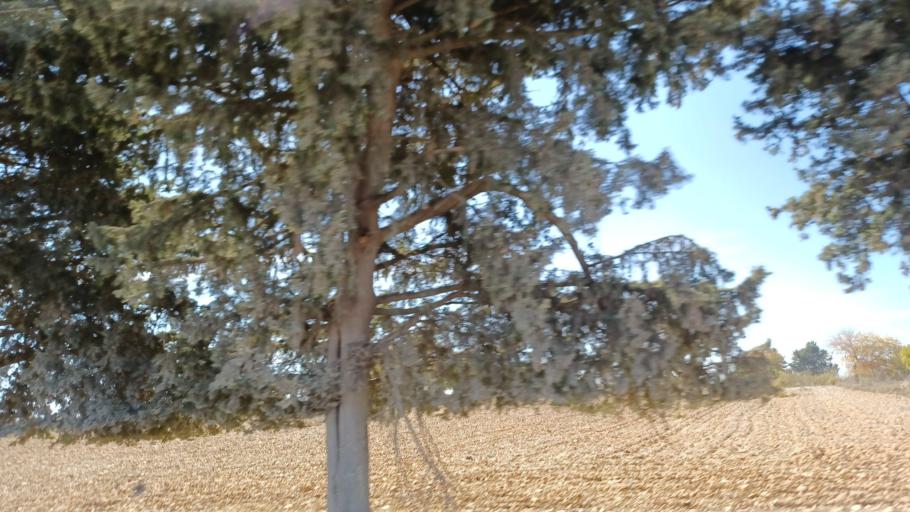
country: CY
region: Pafos
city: Pegeia
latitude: 34.9427
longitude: 32.4063
